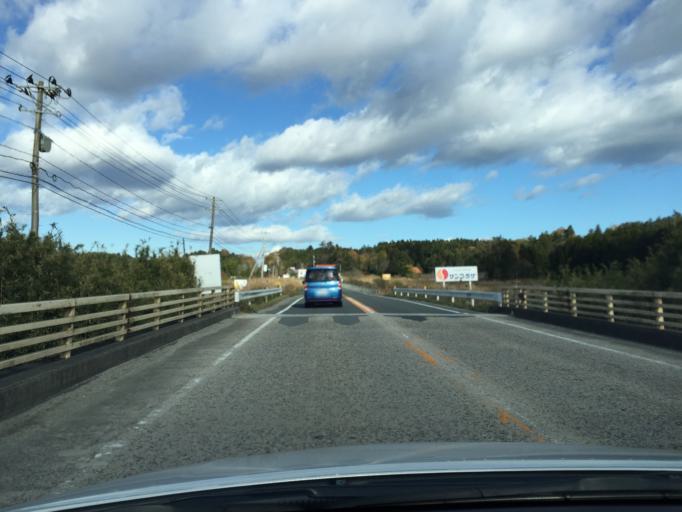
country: JP
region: Fukushima
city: Namie
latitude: 37.4671
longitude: 141.0094
